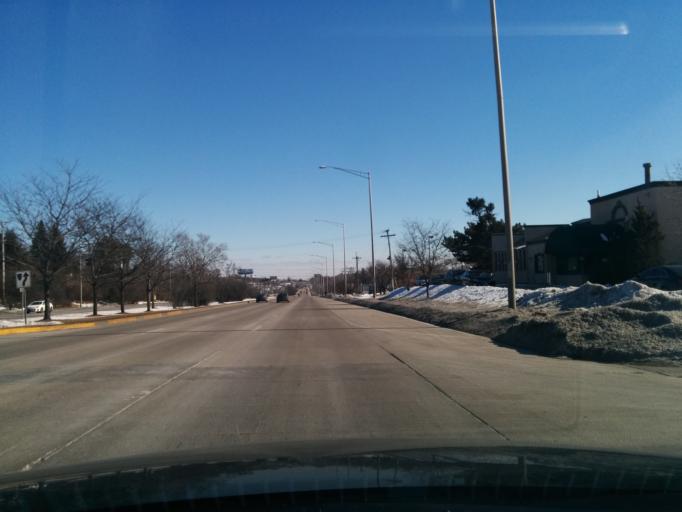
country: US
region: Illinois
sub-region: DuPage County
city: Glendale Heights
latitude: 41.9034
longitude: -88.0583
